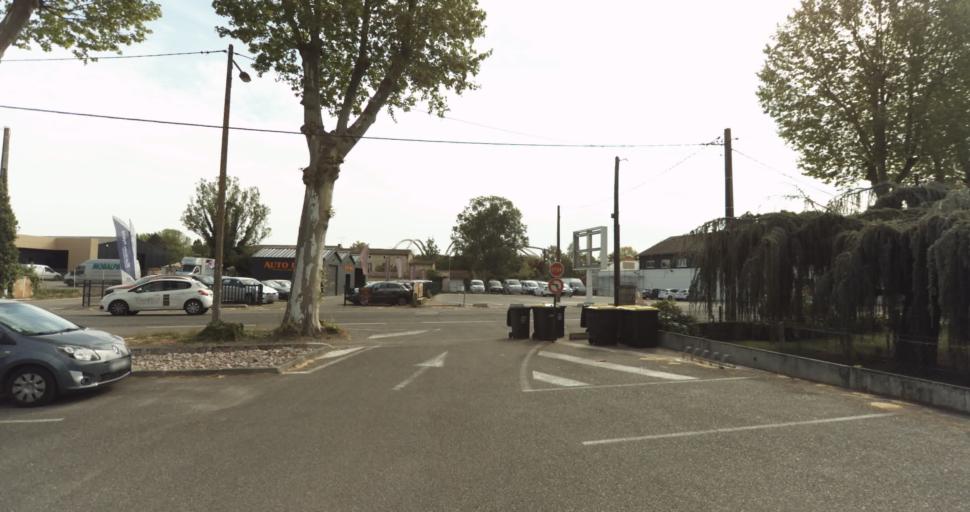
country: FR
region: Aquitaine
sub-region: Departement du Lot-et-Garonne
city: Agen
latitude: 44.1865
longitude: 0.6203
